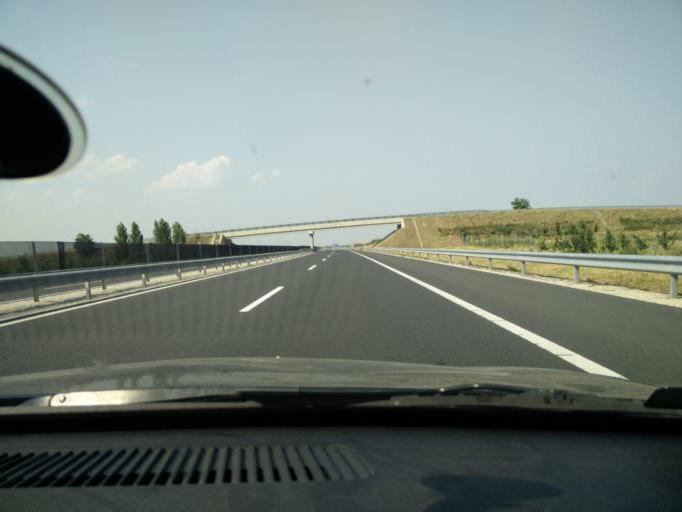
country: HU
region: Tolna
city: Dunaszentgyorgy
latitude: 46.5004
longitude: 18.7665
